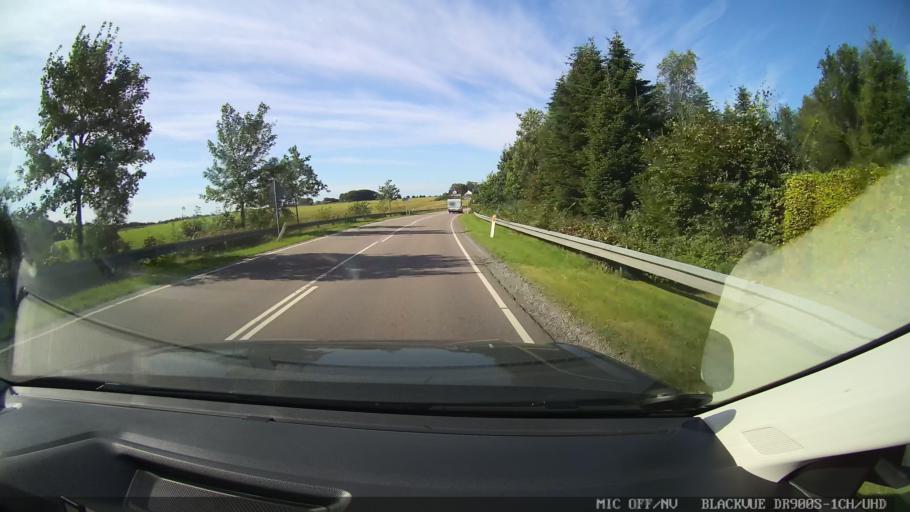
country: DK
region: North Denmark
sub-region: Mariagerfjord Kommune
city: Hobro
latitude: 56.6709
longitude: 9.8451
